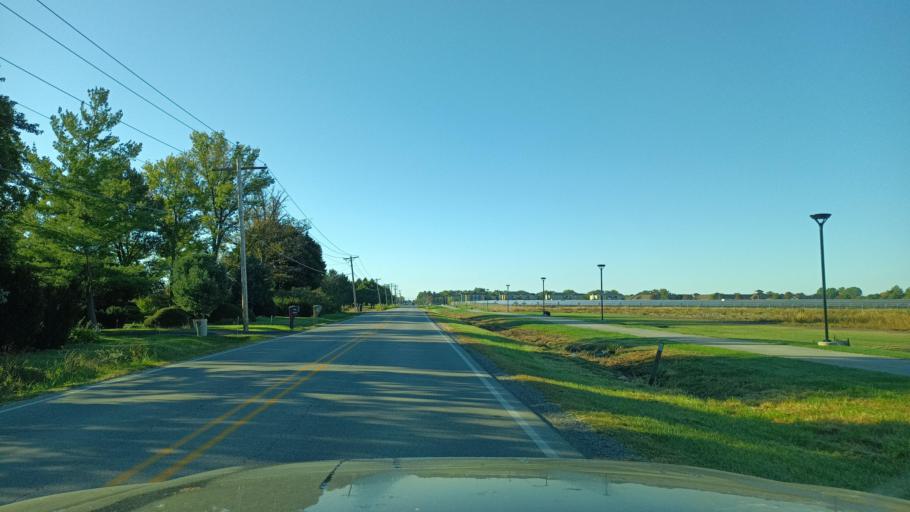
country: US
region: Illinois
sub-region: Champaign County
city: Savoy
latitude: 40.0737
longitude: -88.2385
